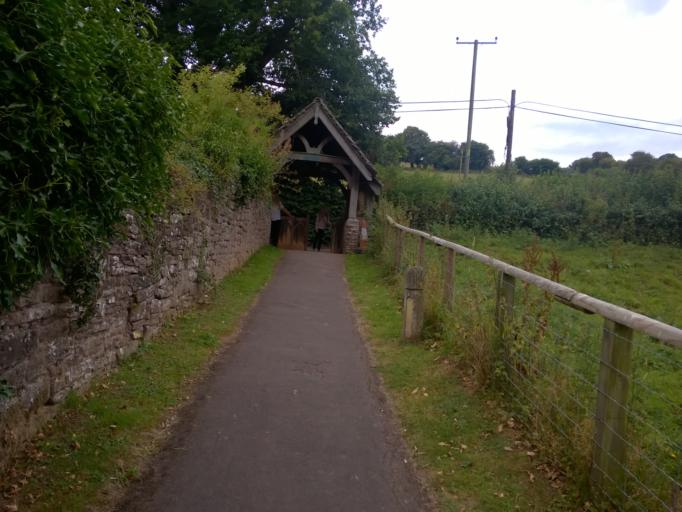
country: GB
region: England
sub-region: Herefordshire
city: Abbey Dore
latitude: 51.9680
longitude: -2.8942
